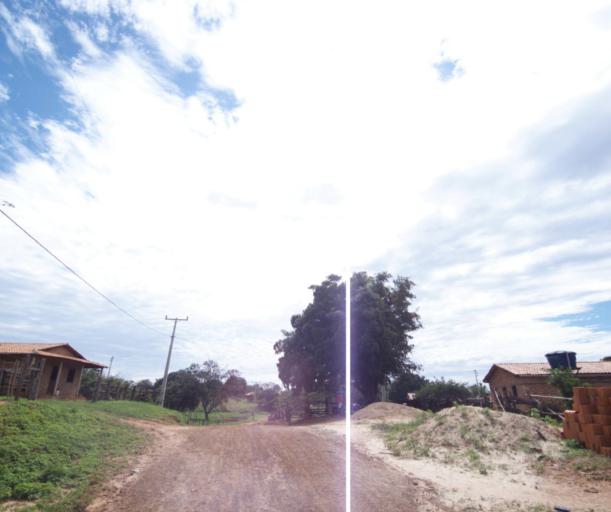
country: BR
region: Bahia
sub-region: Carinhanha
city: Carinhanha
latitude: -14.2362
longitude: -44.4054
